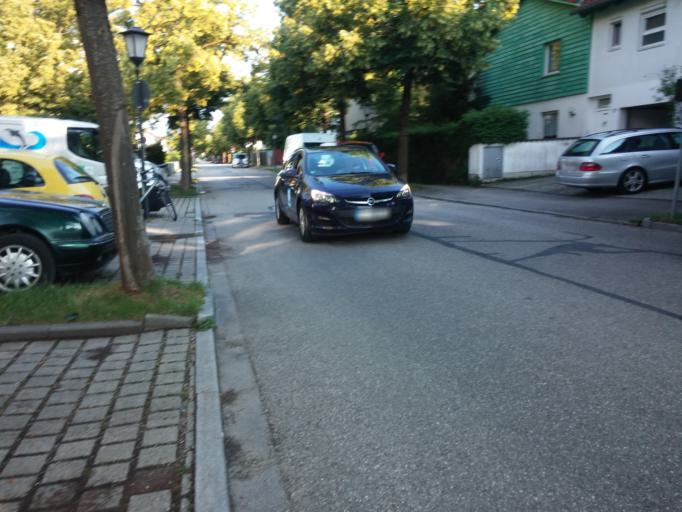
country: DE
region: Bavaria
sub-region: Upper Bavaria
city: Feldkirchen
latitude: 48.1509
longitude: 11.7319
